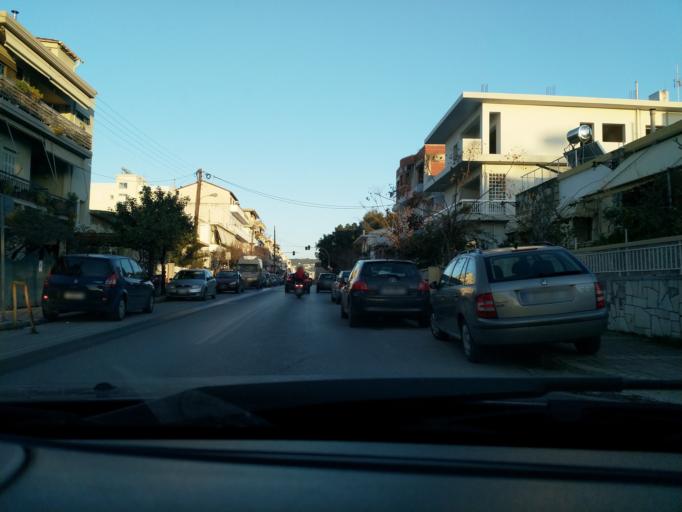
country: GR
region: Crete
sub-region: Nomos Chanias
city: Chania
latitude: 35.5101
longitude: 24.0128
